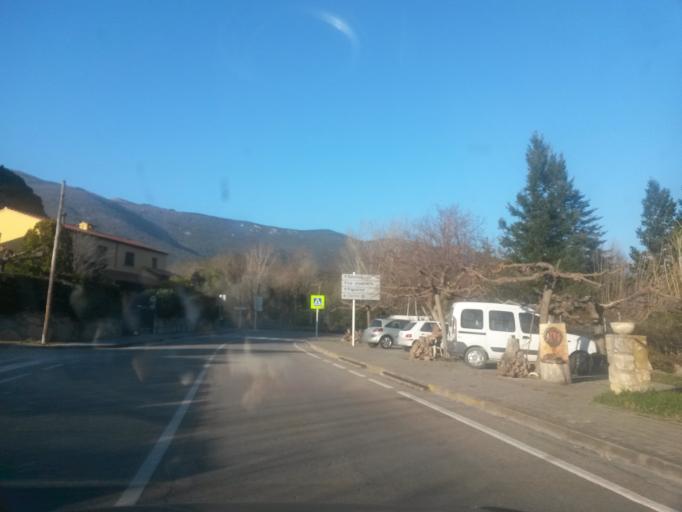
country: ES
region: Catalonia
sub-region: Provincia de Girona
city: Macanet de Cabrenys
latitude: 42.3852
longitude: 2.7536
